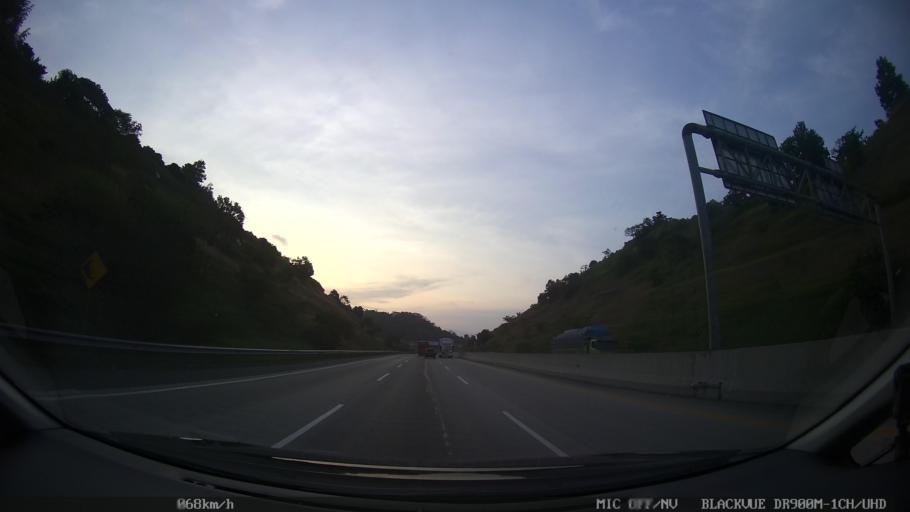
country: ID
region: Lampung
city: Penengahan
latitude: -5.8615
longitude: 105.7374
